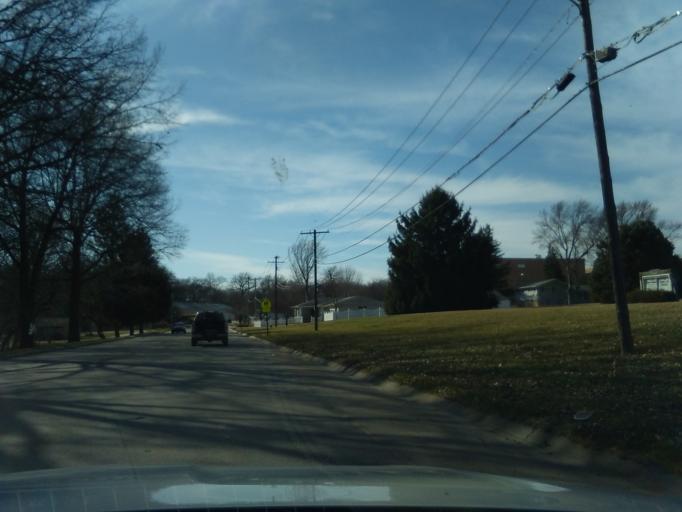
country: US
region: Nebraska
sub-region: Otoe County
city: Nebraska City
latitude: 40.6770
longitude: -95.8765
